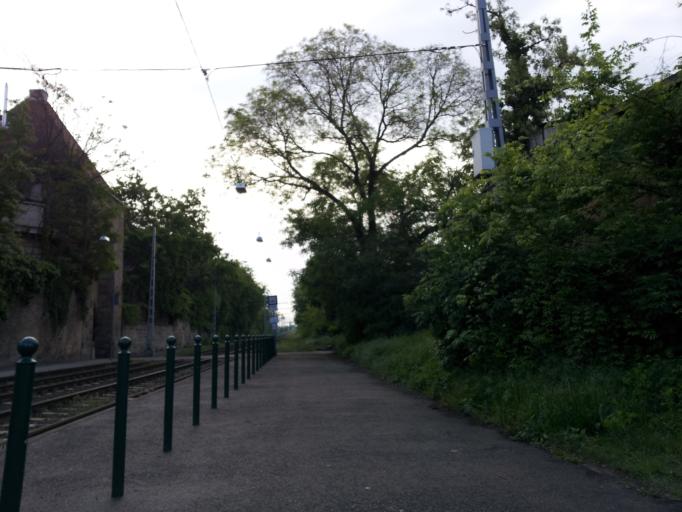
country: HU
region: Budapest
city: Budapest VIII. keruelet
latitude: 47.4912
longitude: 19.0964
